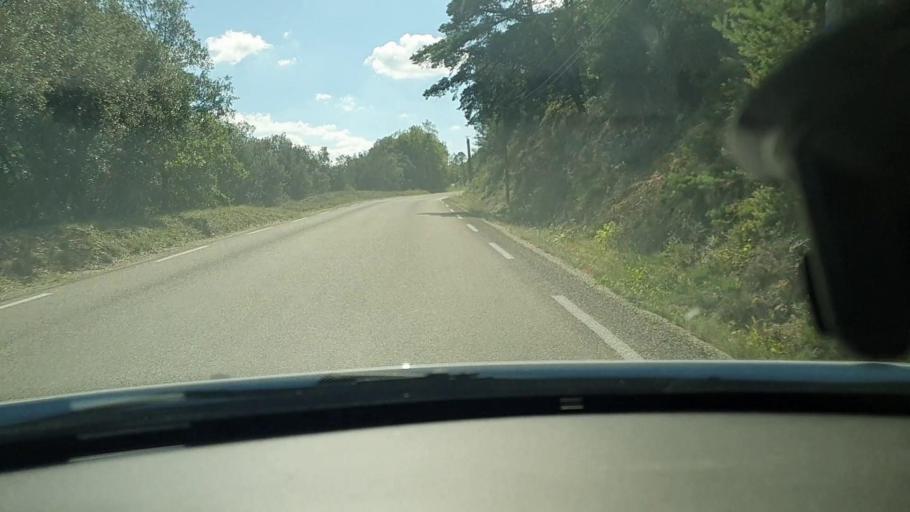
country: FR
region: Languedoc-Roussillon
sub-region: Departement du Gard
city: Goudargues
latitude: 44.1728
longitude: 4.4881
